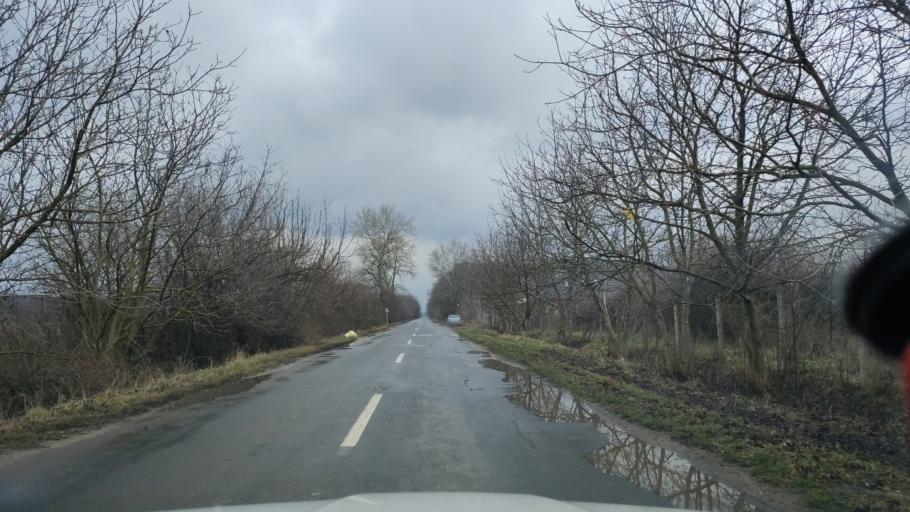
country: HU
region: Hajdu-Bihar
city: Hajduszoboszlo
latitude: 47.4605
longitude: 21.4004
